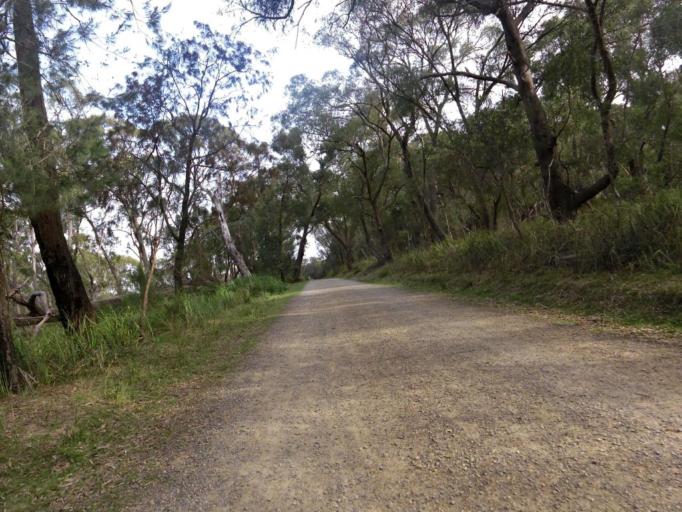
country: AU
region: Victoria
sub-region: Yarra Ranges
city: Lysterfield
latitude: -37.9621
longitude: 145.2938
